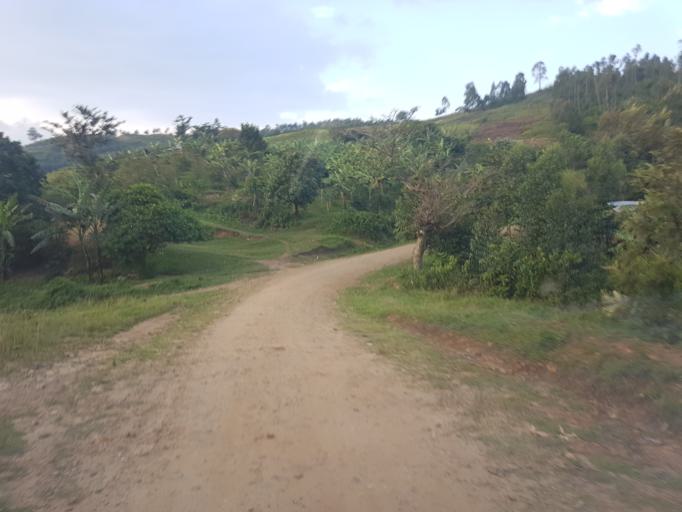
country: UG
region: Western Region
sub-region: Mitoma District
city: Mitoma
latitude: -0.6805
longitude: 29.9117
